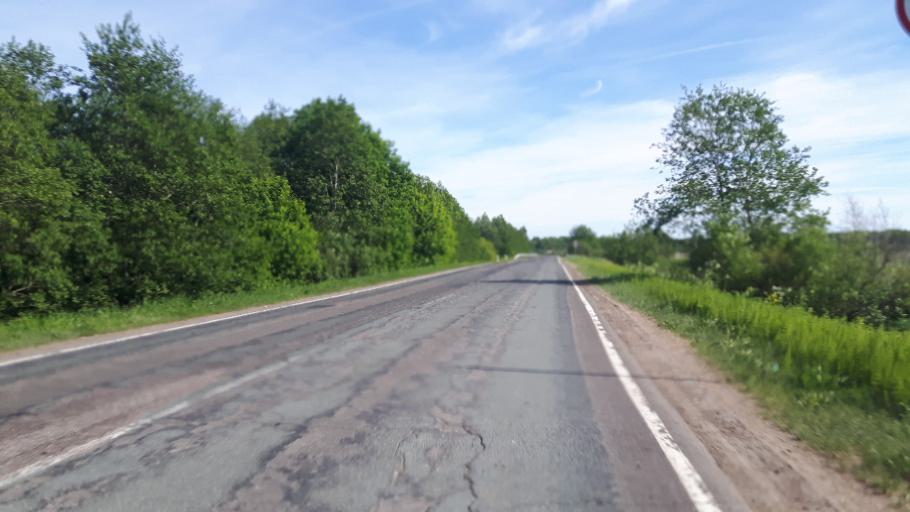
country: RU
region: Leningrad
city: Ivangorod
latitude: 59.4181
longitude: 28.3239
